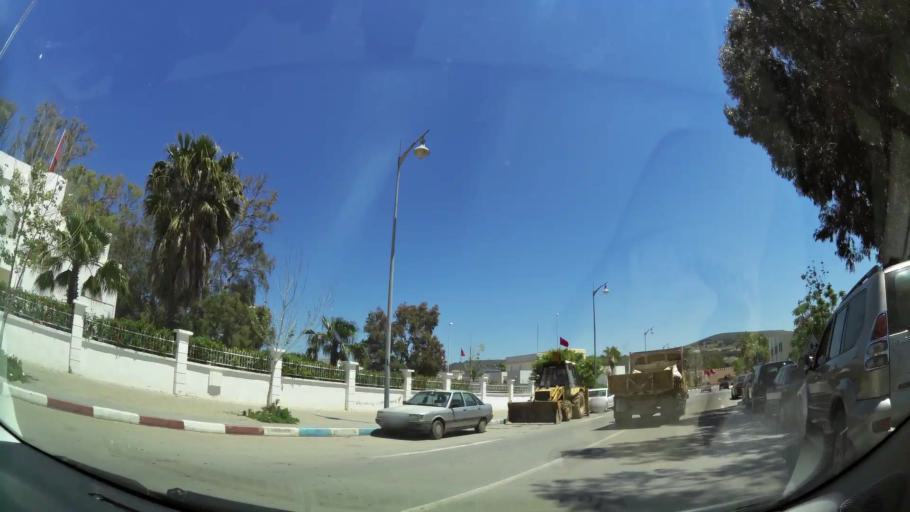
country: MA
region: Oriental
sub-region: Berkane-Taourirt
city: Madagh
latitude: 35.0812
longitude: -2.2171
